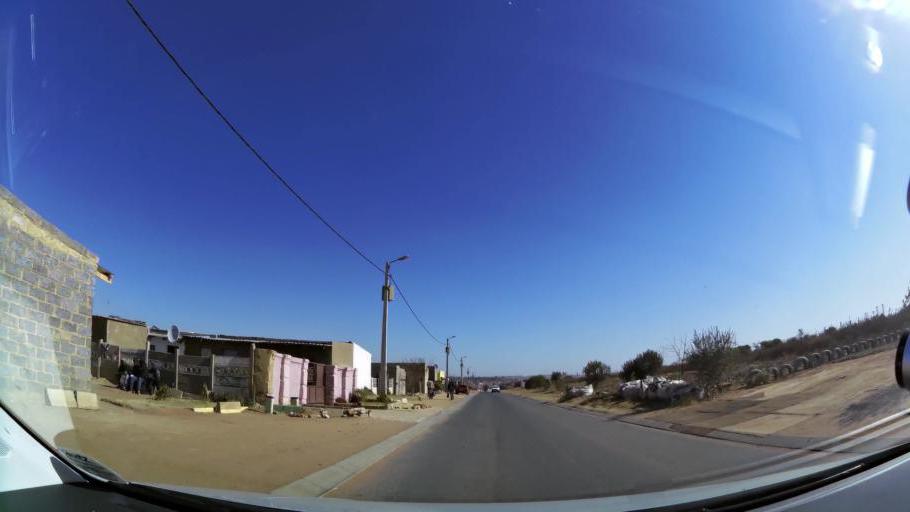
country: ZA
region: Gauteng
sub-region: Ekurhuleni Metropolitan Municipality
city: Tembisa
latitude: -26.0318
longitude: 28.2297
